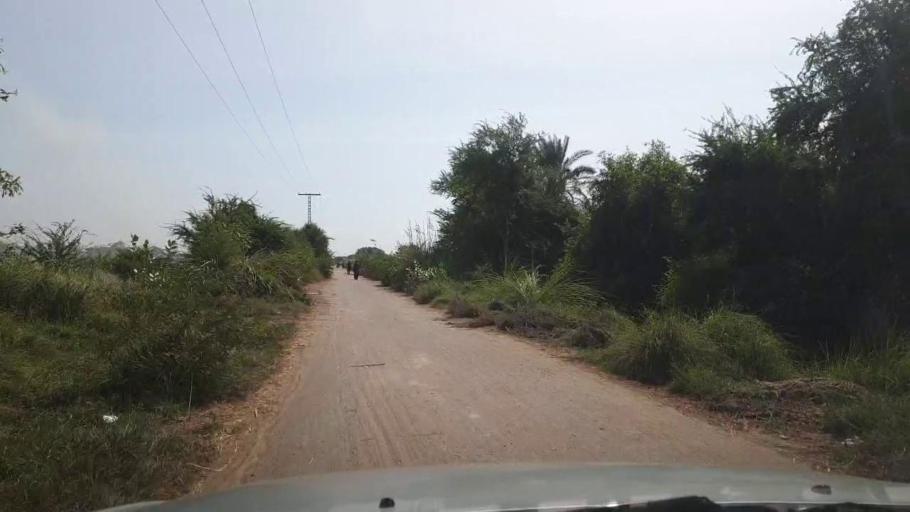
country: PK
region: Sindh
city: Tando Muhammad Khan
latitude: 25.1494
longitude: 68.3916
